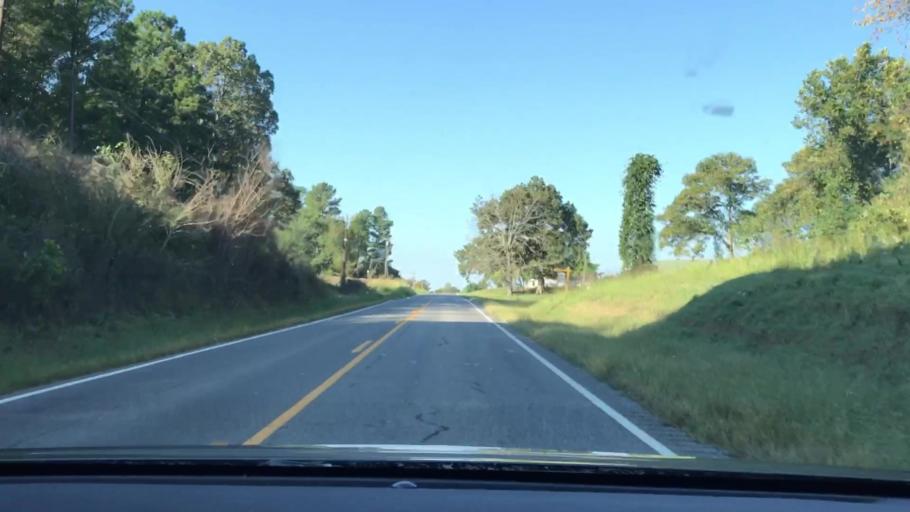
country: US
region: Kentucky
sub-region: Marshall County
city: Benton
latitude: 36.7688
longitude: -88.1773
